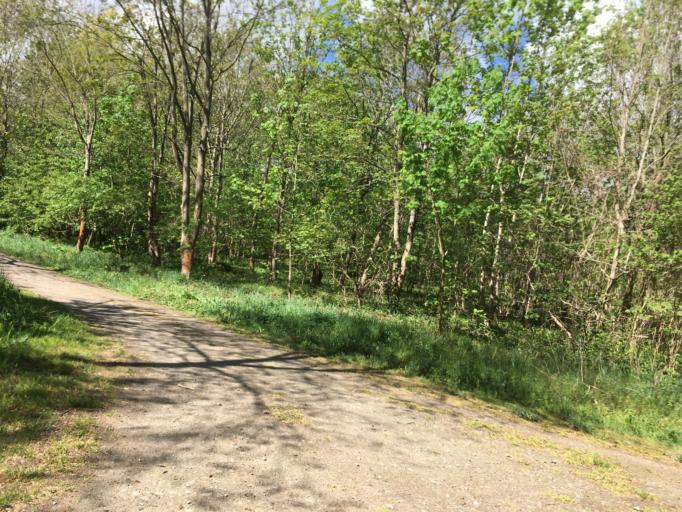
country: DE
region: Berlin
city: Blankenfelde
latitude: 52.6248
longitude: 13.3899
